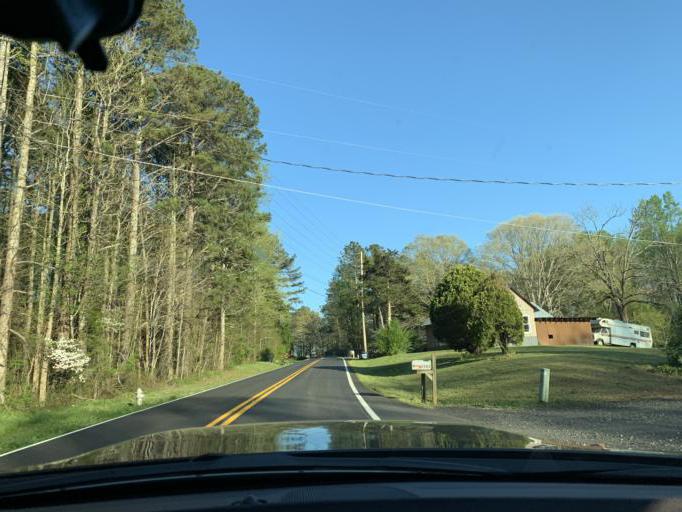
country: US
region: Georgia
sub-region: Forsyth County
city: Cumming
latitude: 34.2578
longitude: -84.2045
